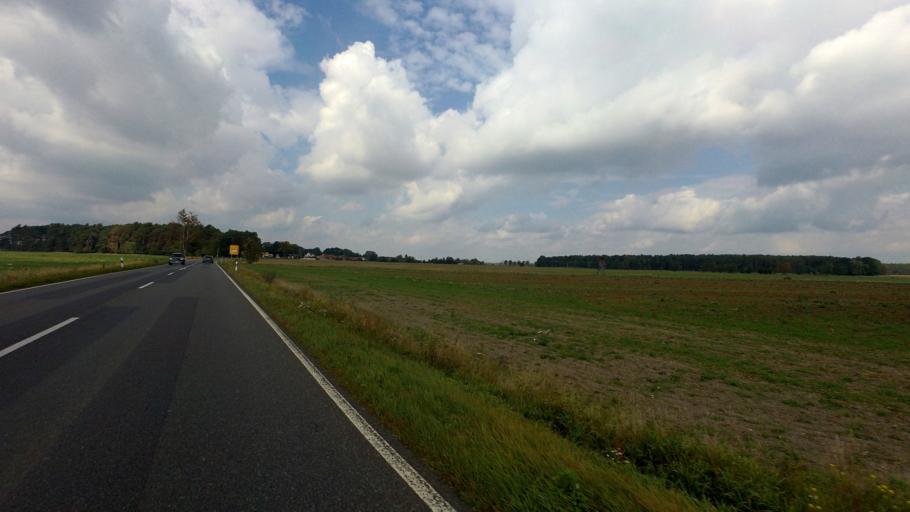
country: DE
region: Saxony-Anhalt
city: Holzdorf
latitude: 51.7925
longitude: 13.1831
